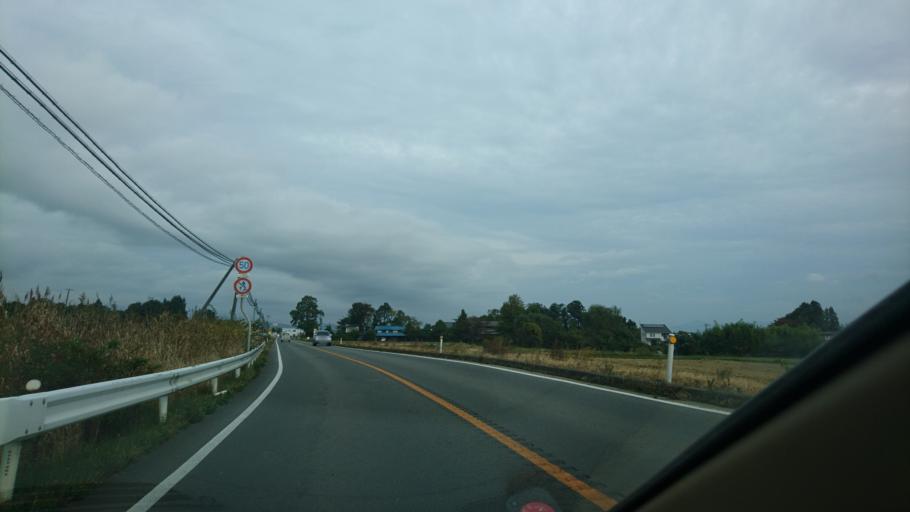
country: JP
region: Iwate
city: Morioka-shi
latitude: 39.6243
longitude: 141.1201
